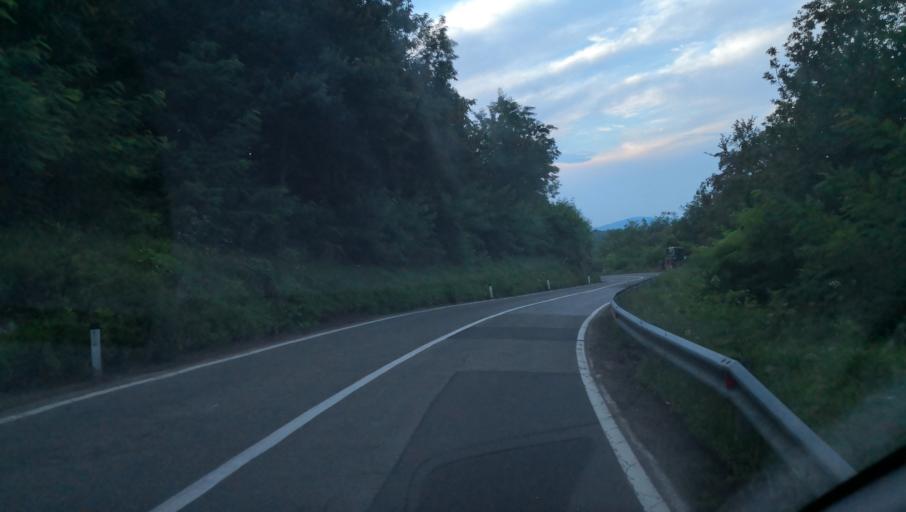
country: SI
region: Semic
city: Semic
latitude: 45.7044
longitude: 15.2462
